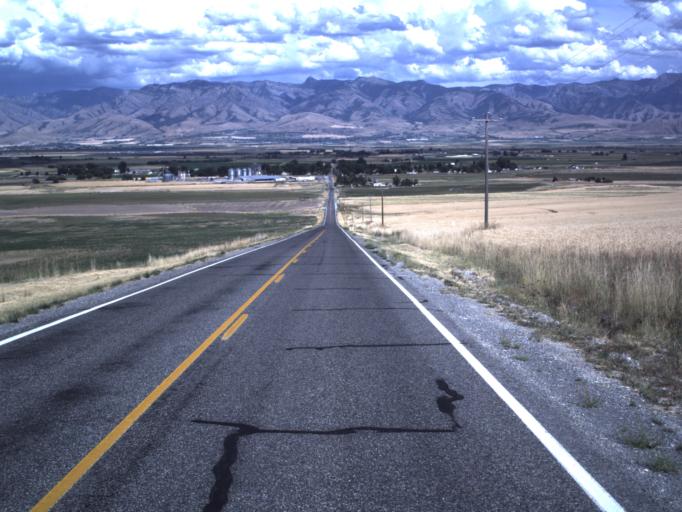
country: US
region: Utah
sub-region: Cache County
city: Lewiston
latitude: 41.9175
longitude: -111.9715
